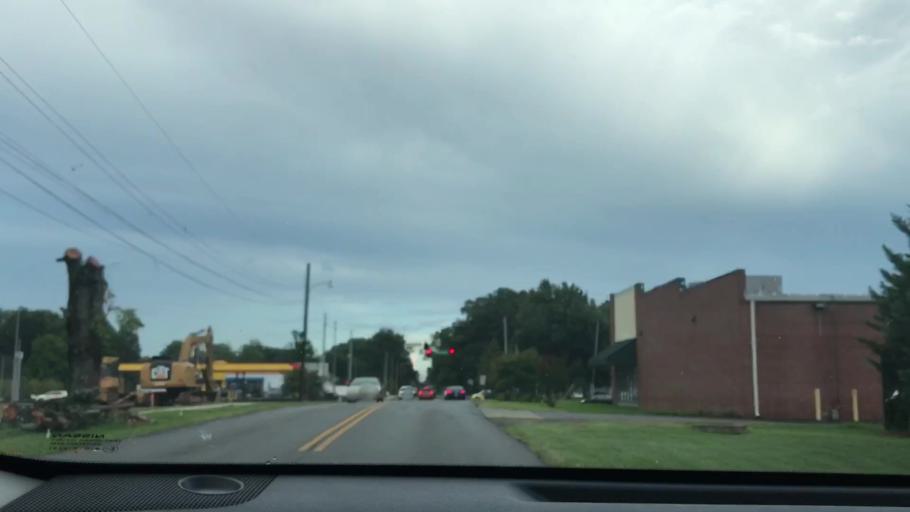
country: US
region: Kentucky
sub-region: Calloway County
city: Murray
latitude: 36.6029
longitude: -88.3165
